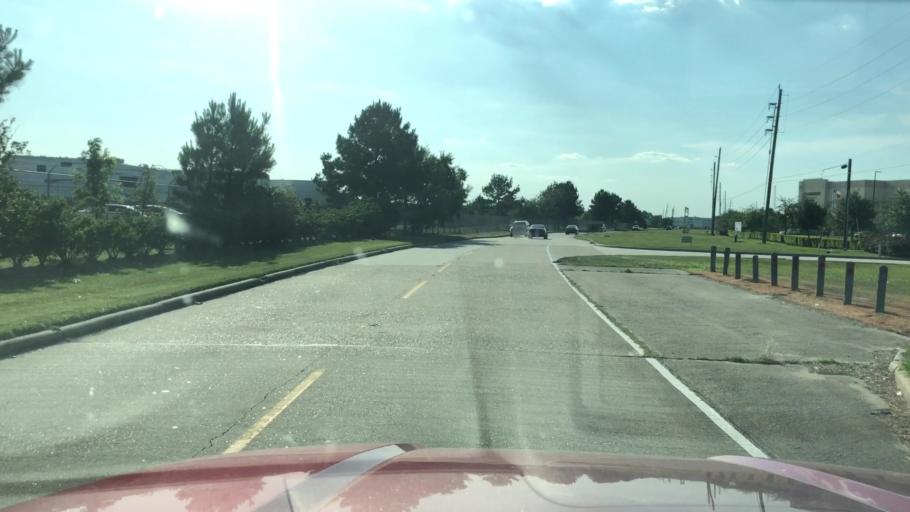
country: US
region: Texas
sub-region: Harris County
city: Hudson
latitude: 29.9427
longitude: -95.4898
